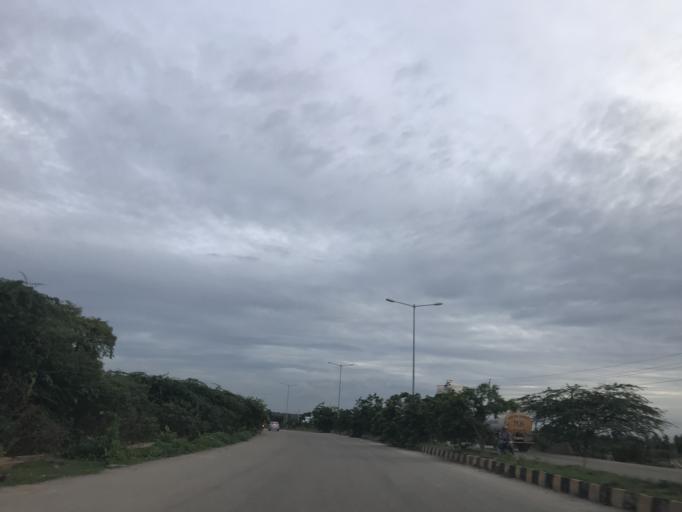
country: IN
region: Karnataka
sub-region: Bangalore Rural
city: Devanhalli
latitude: 13.1844
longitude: 77.7155
